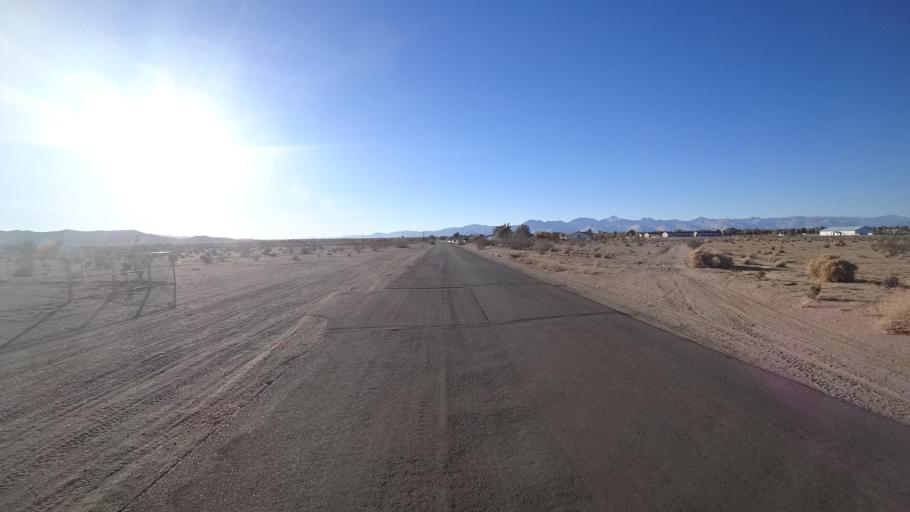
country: US
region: California
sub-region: Kern County
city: Ridgecrest
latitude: 35.6008
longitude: -117.6660
